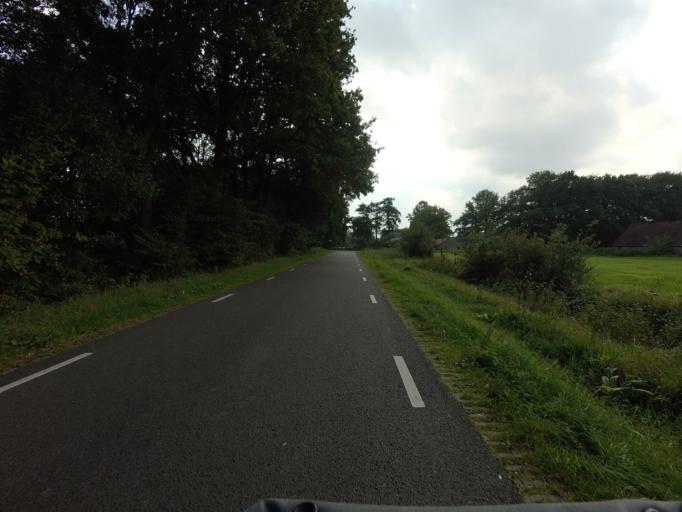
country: NL
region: Utrecht
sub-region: Gemeente Amersfoort
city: Hoogland
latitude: 52.1662
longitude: 5.3457
